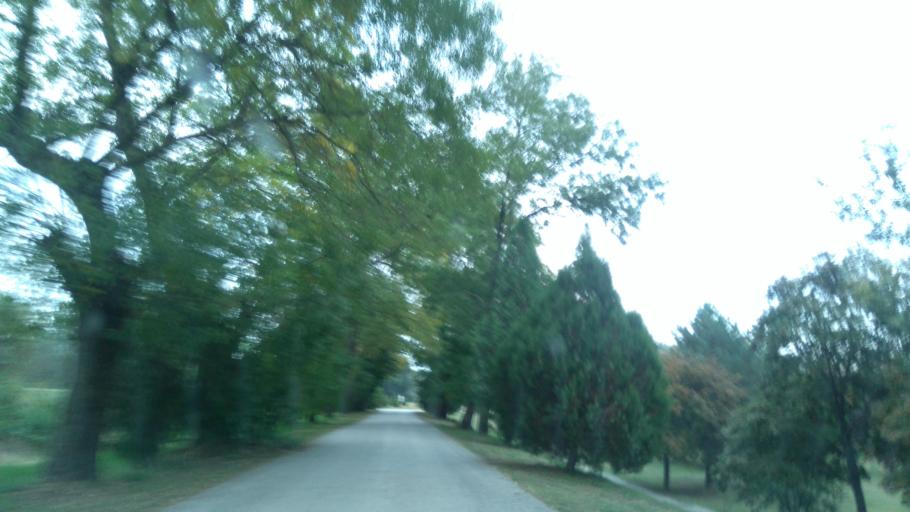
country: RS
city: Mol
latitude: 45.7645
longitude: 20.1429
